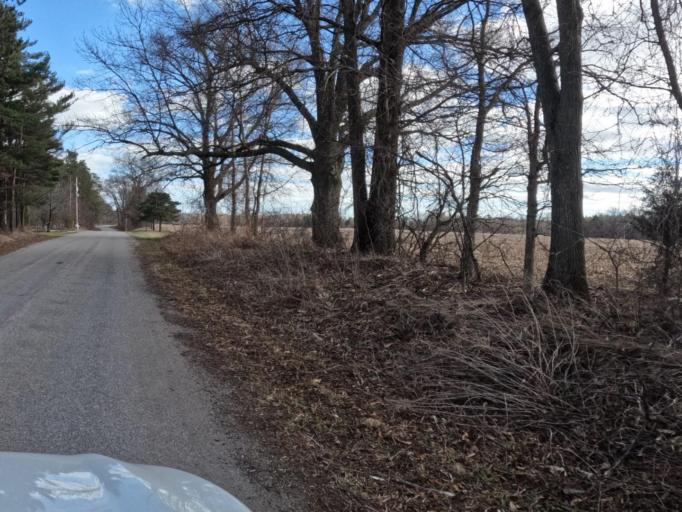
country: CA
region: Ontario
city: Norfolk County
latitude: 42.7487
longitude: -80.2983
